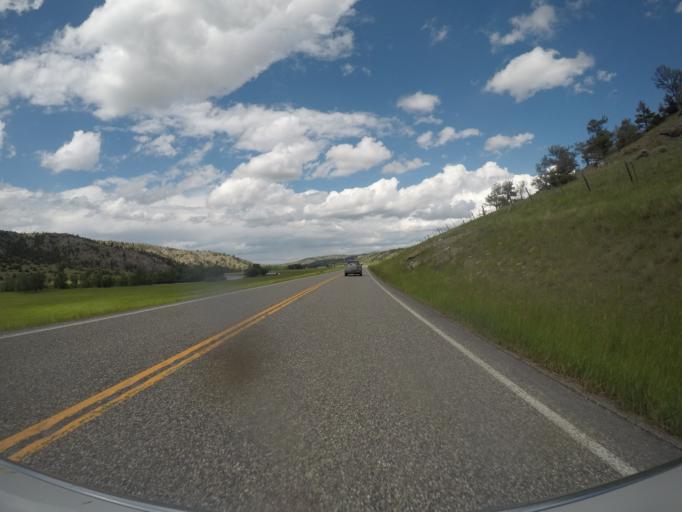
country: US
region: Montana
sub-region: Sweet Grass County
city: Big Timber
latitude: 45.7075
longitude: -110.0110
